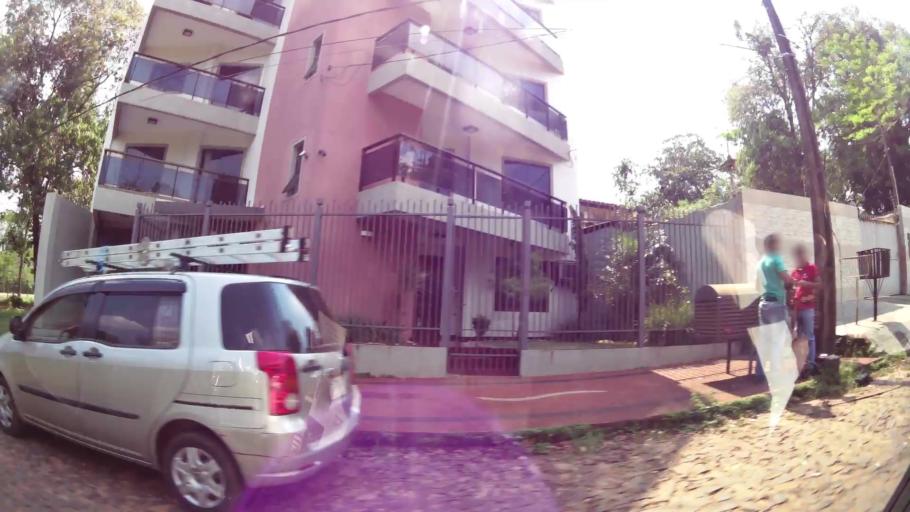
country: PY
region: Alto Parana
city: Ciudad del Este
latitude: -25.5126
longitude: -54.6363
